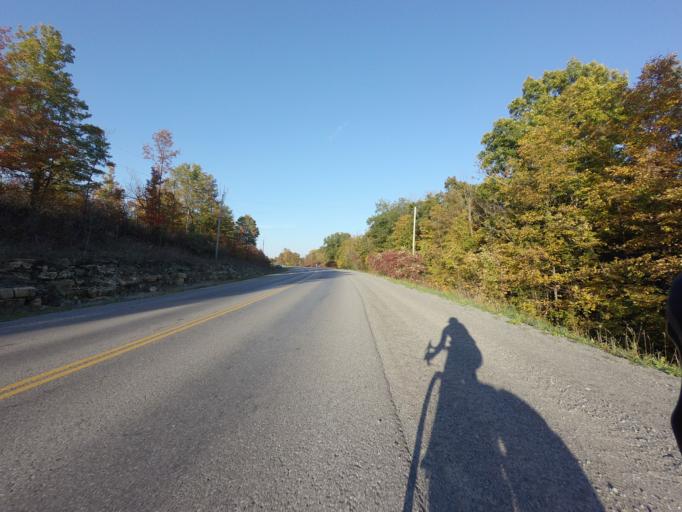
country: CA
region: Ontario
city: Kingston
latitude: 44.3596
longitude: -76.4252
